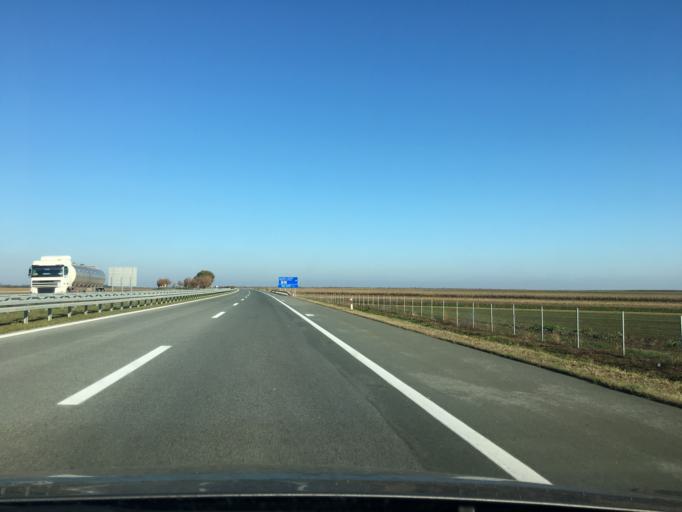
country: RS
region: Autonomna Pokrajina Vojvodina
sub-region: Severnobacki Okrug
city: Mali Igos
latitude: 45.6706
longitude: 19.7286
